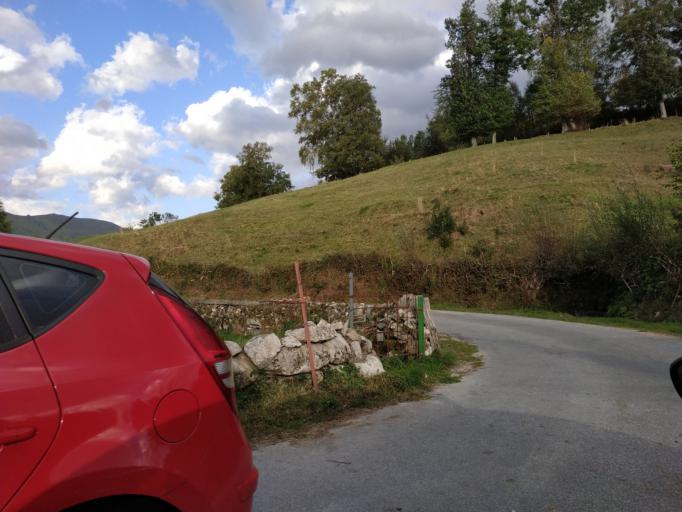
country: ES
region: Castille and Leon
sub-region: Provincia de Leon
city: Candin
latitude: 42.8569
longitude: -6.8747
